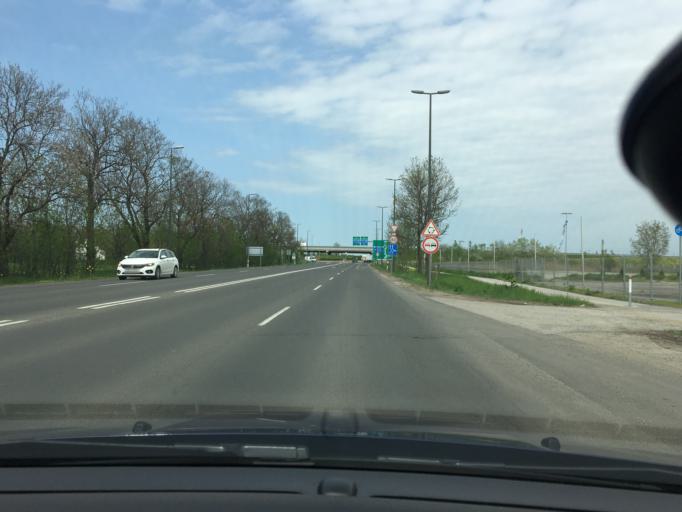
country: HU
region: Csongrad
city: Szeged
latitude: 46.2921
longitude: 20.1751
